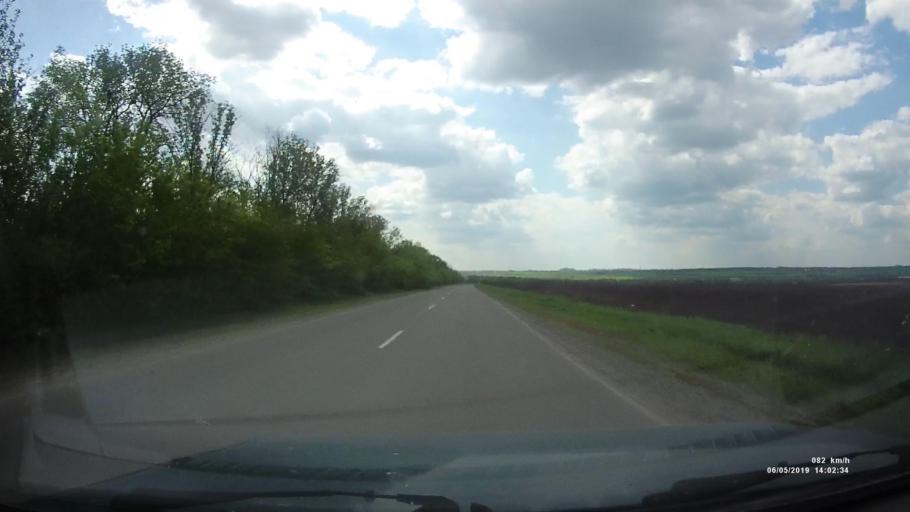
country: RU
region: Rostov
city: Shakhty
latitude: 47.6821
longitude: 40.3613
